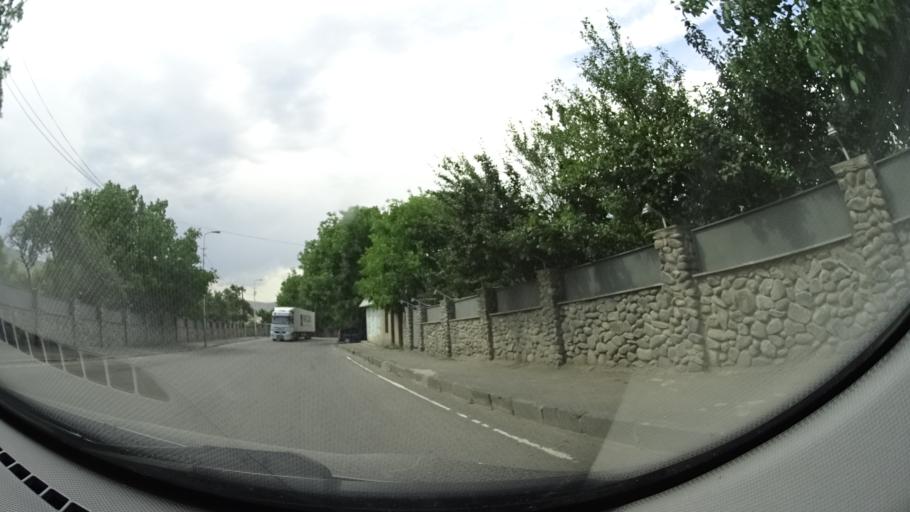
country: GE
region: Samtskhe-Javakheti
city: Aspindza
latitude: 41.5715
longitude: 43.2532
